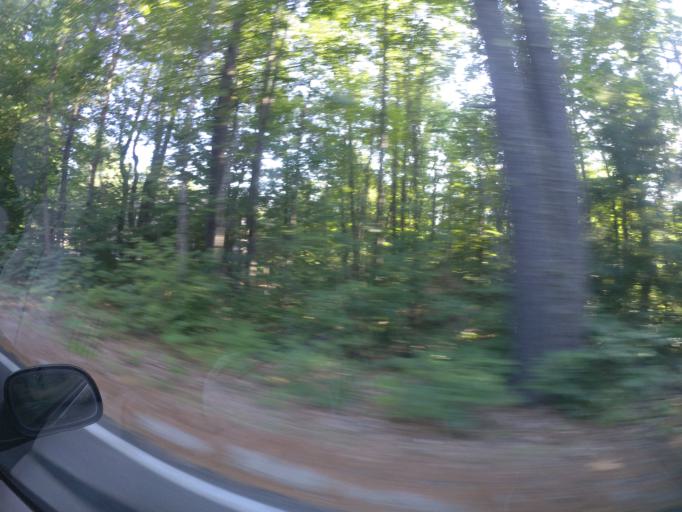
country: US
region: Maine
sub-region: Cumberland County
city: Raymond
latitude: 43.8911
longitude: -70.4389
